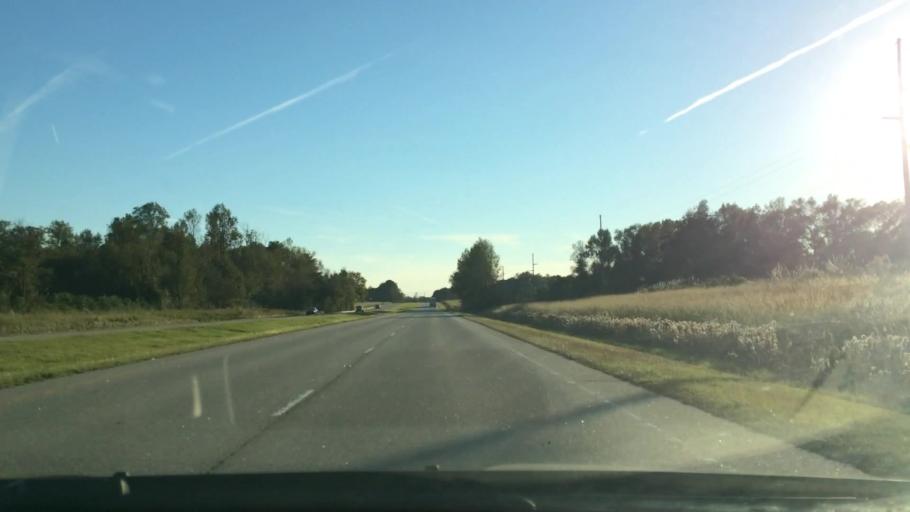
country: US
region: North Carolina
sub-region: Pitt County
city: Grifton
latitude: 35.4015
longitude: -77.4382
